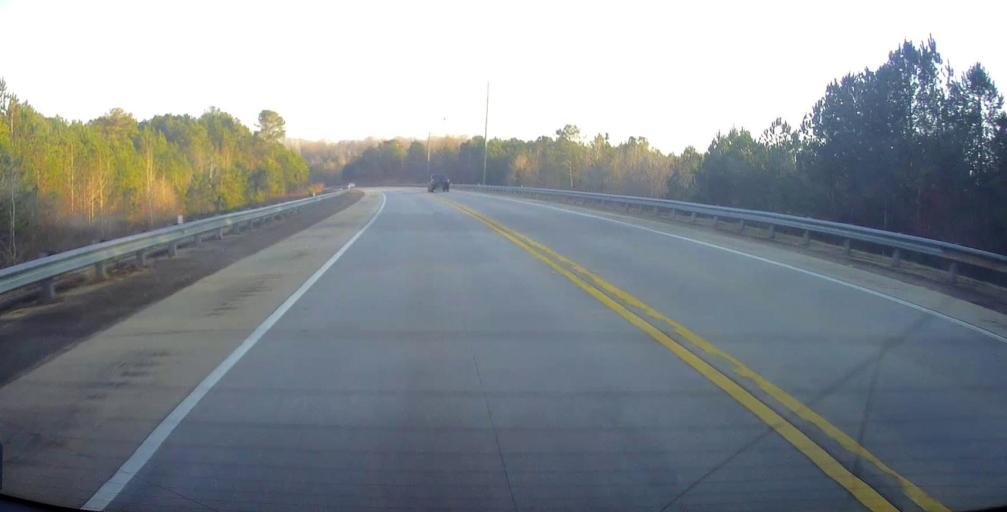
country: US
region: Georgia
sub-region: Troup County
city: La Grange
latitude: 32.9977
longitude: -85.0838
